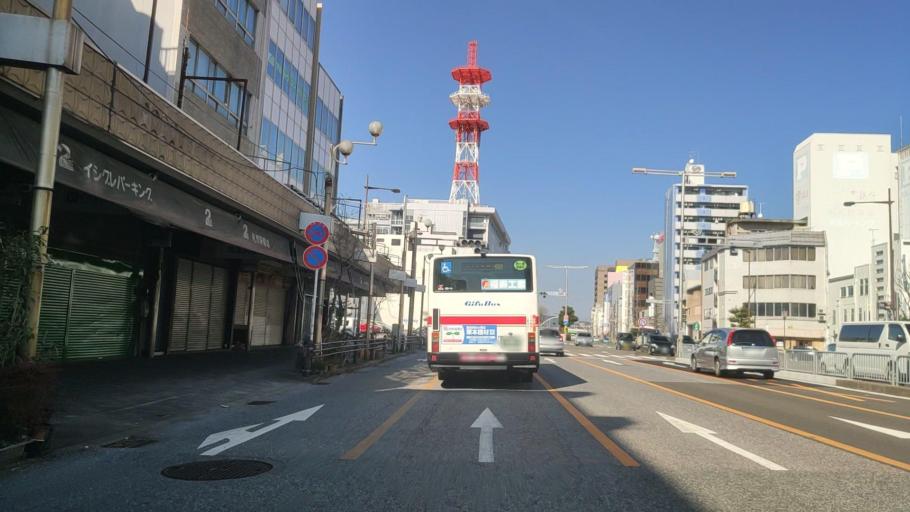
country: JP
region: Gifu
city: Gifu-shi
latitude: 35.4199
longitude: 136.7573
